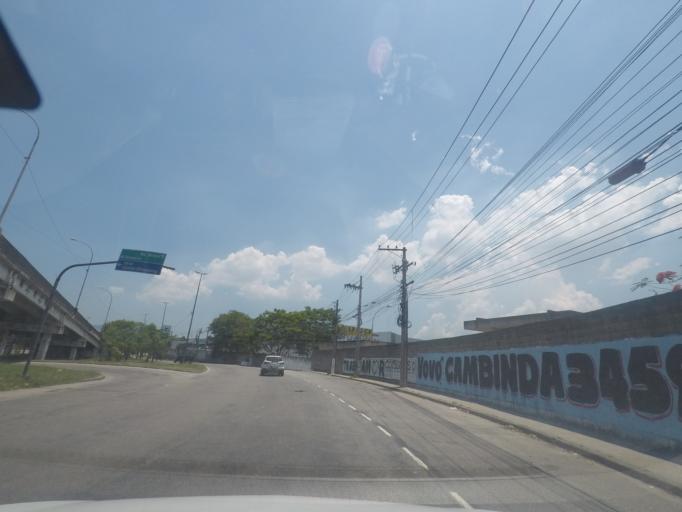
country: BR
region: Rio de Janeiro
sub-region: Duque De Caxias
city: Duque de Caxias
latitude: -22.8021
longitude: -43.3058
